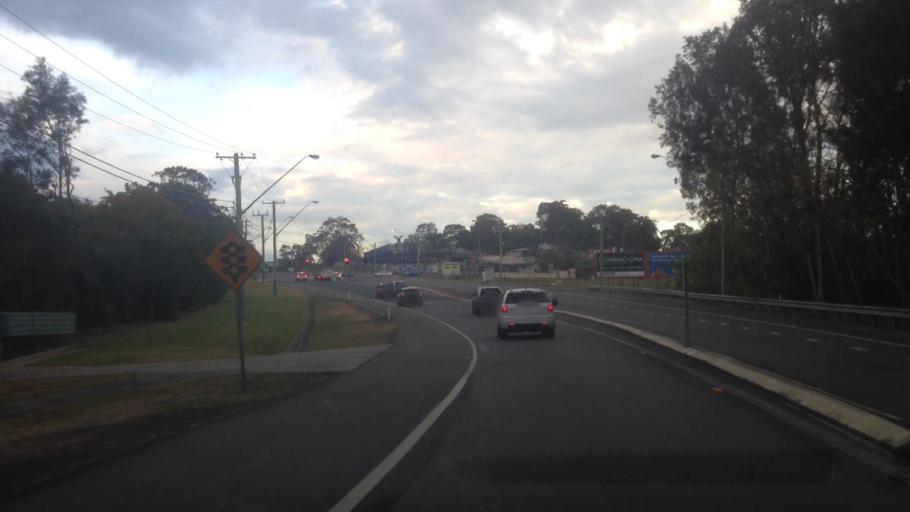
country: AU
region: New South Wales
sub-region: Wyong Shire
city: Kanwal
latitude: -33.2633
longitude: 151.4795
